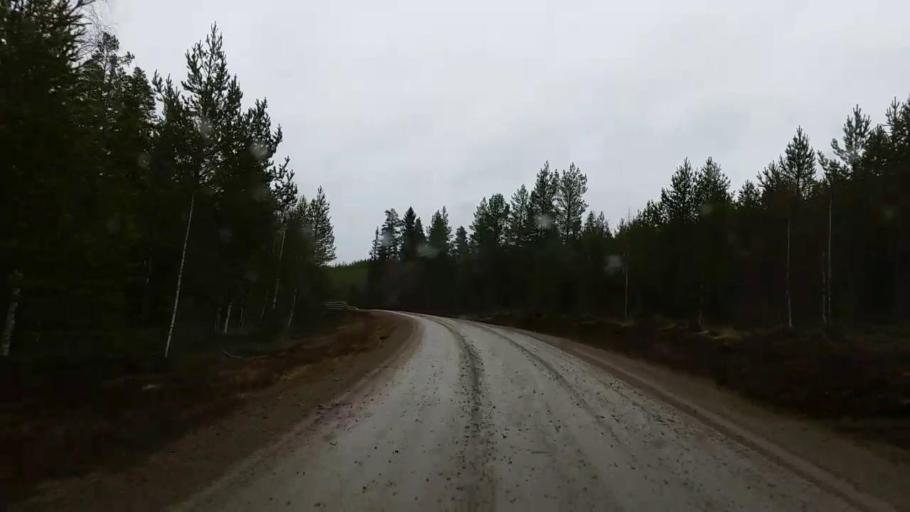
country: SE
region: Gaevleborg
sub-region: Ljusdals Kommun
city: Farila
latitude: 62.1145
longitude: 15.6920
